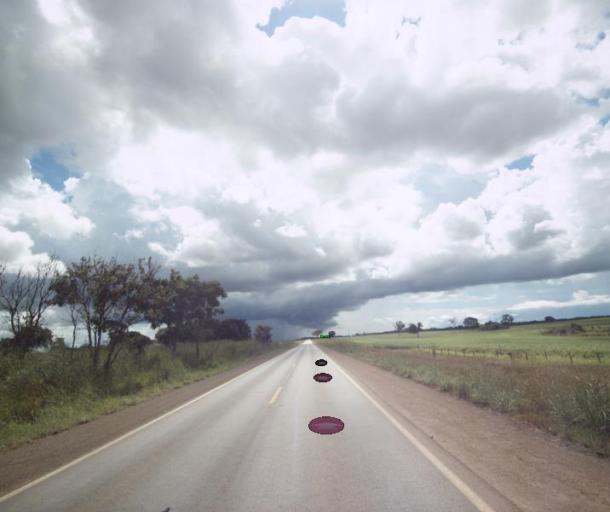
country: BR
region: Goias
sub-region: Uruacu
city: Uruacu
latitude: -14.6994
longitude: -49.1098
